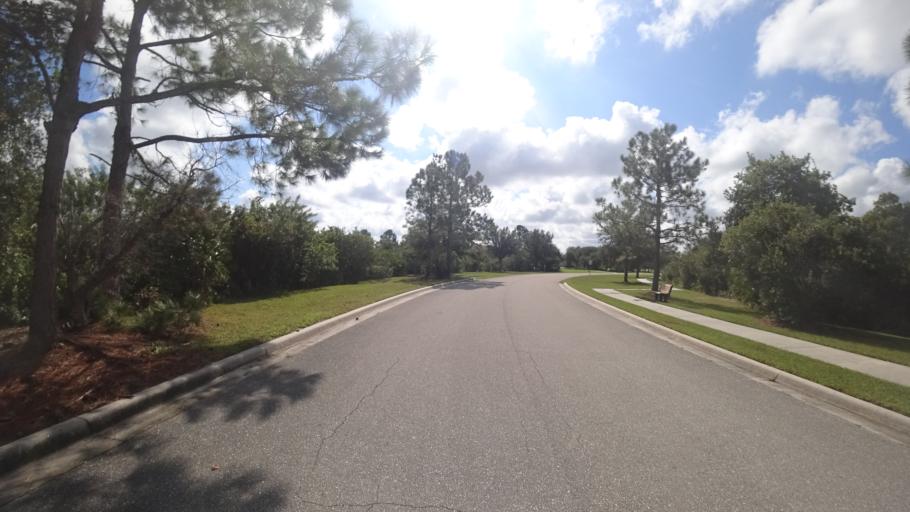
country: US
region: Florida
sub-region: Sarasota County
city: Fruitville
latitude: 27.3960
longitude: -82.3063
